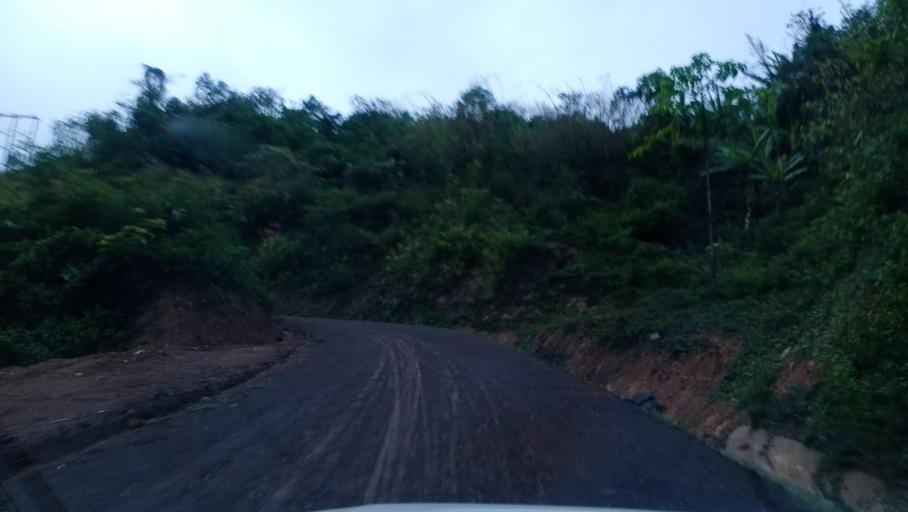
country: LA
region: Phongsali
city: Khoa
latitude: 21.2291
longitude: 102.6907
